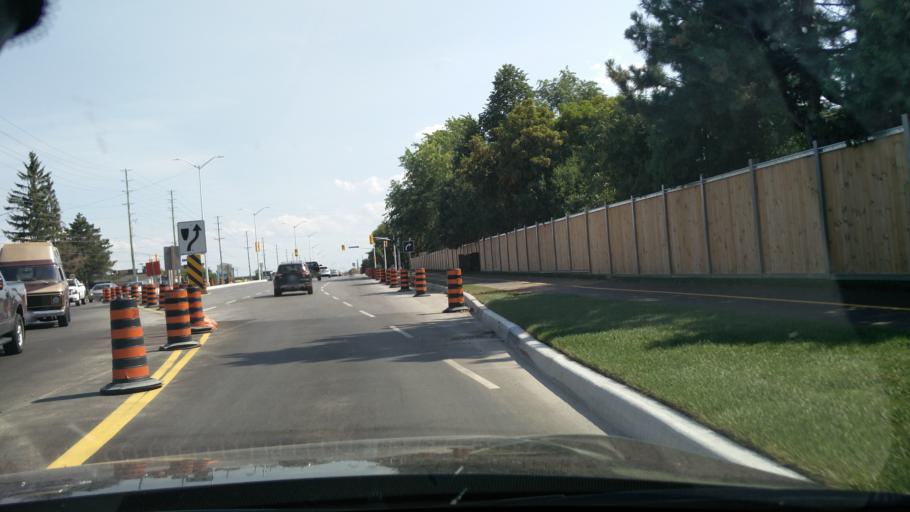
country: CA
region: Ontario
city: Bells Corners
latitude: 45.2761
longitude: -75.7499
